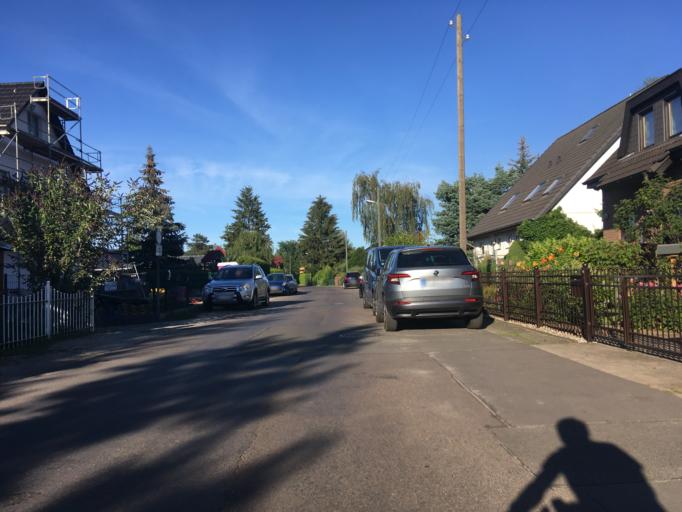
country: DE
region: Berlin
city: Grunau
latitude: 52.4258
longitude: 13.5665
